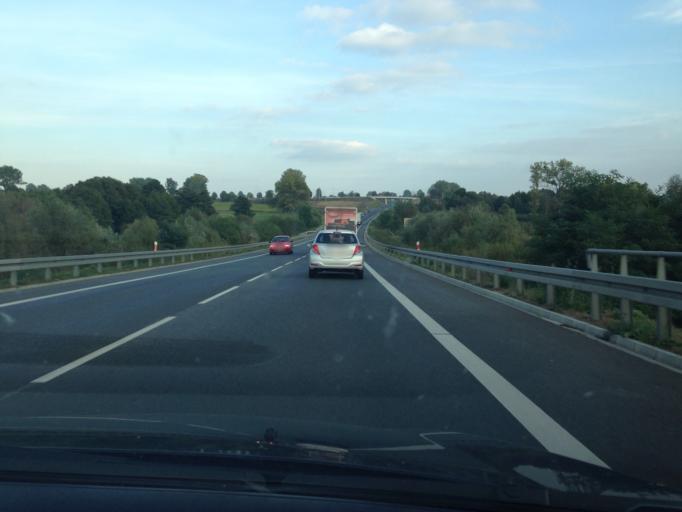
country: PL
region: Greater Poland Voivodeship
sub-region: Powiat gnieznienski
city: Niechanowo
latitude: 52.5558
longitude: 17.6882
